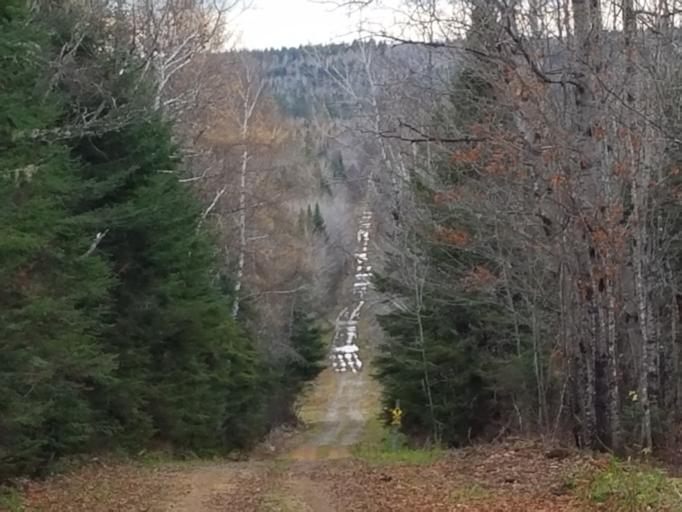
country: US
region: Maine
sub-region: Aroostook County
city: Caribou
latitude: 46.8433
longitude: -68.2517
